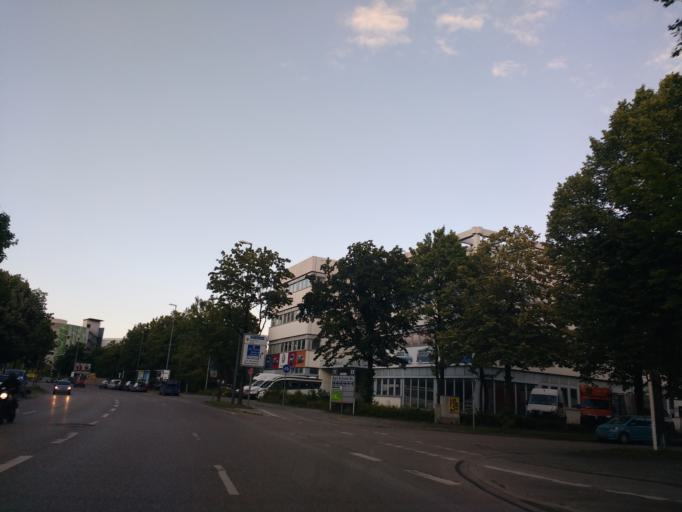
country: DE
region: Bavaria
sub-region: Upper Bavaria
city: Bogenhausen
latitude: 48.1350
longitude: 11.6661
